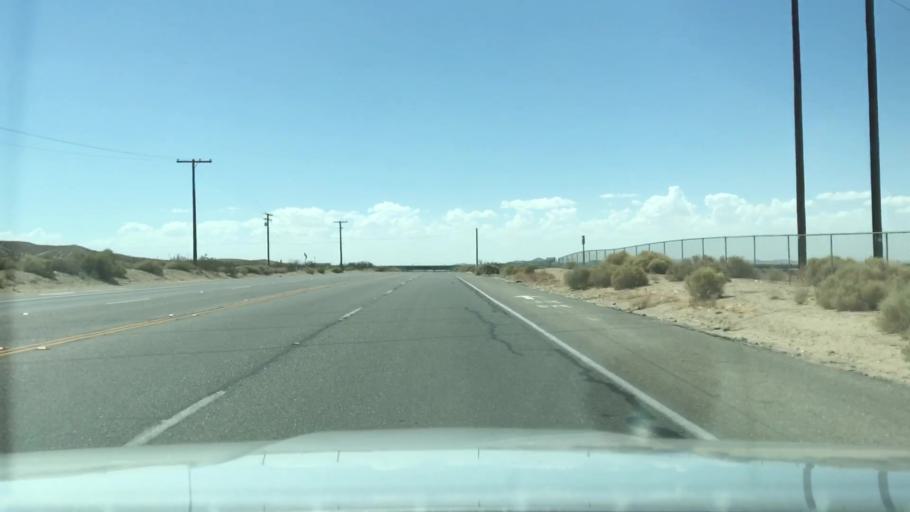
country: US
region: California
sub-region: San Bernardino County
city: Lenwood
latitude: 34.8855
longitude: -117.0813
